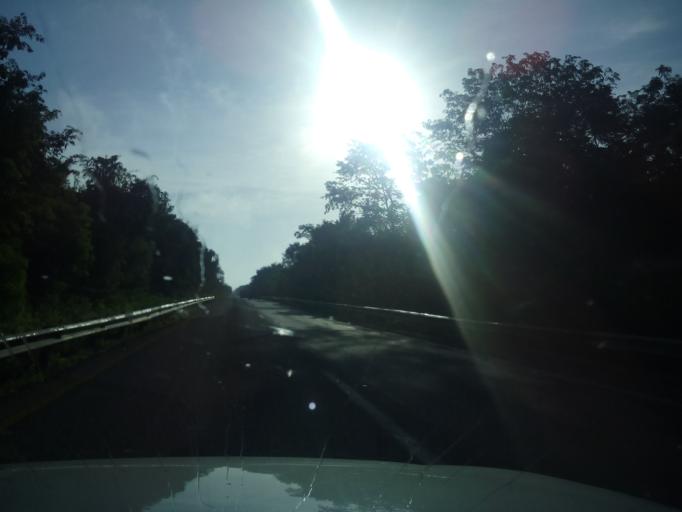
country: MX
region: Yucatan
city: Piste
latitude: 20.7428
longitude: -88.6732
